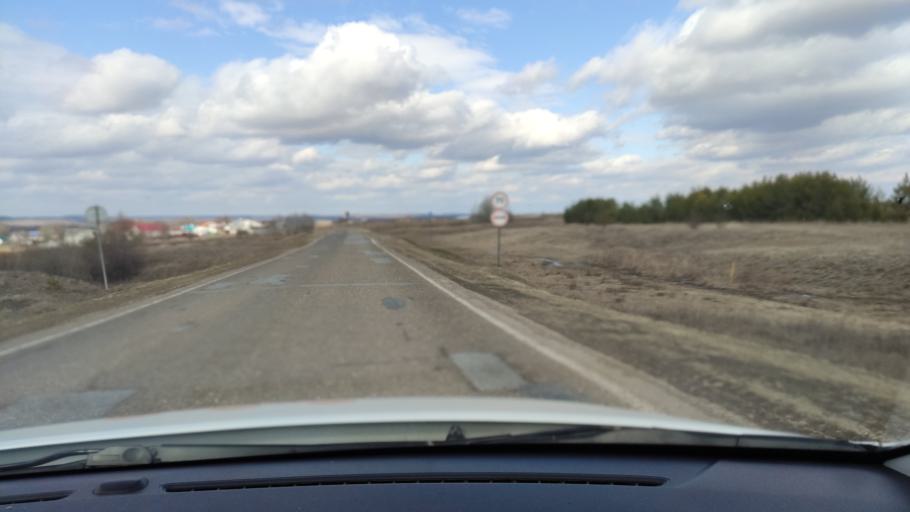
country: RU
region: Tatarstan
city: Vysokaya Gora
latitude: 56.1710
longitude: 49.2138
